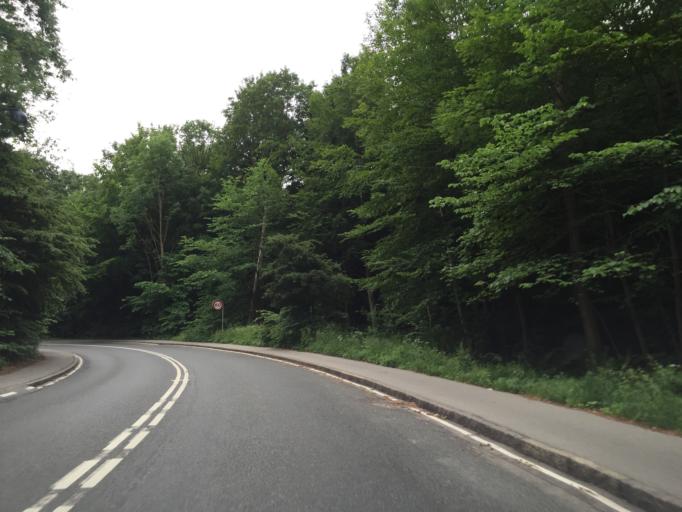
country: DK
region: Capital Region
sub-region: Lyngby-Tarbaek Kommune
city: Kongens Lyngby
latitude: 55.7696
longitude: 12.5355
